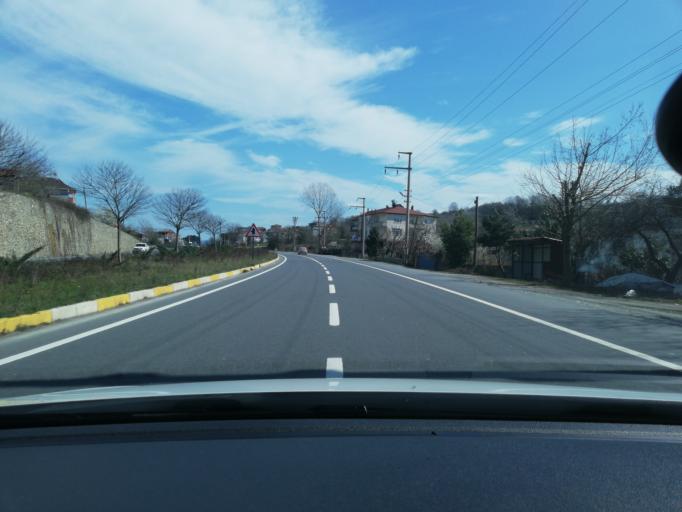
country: TR
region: Duzce
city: Akcakoca
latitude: 41.0964
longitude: 31.2184
